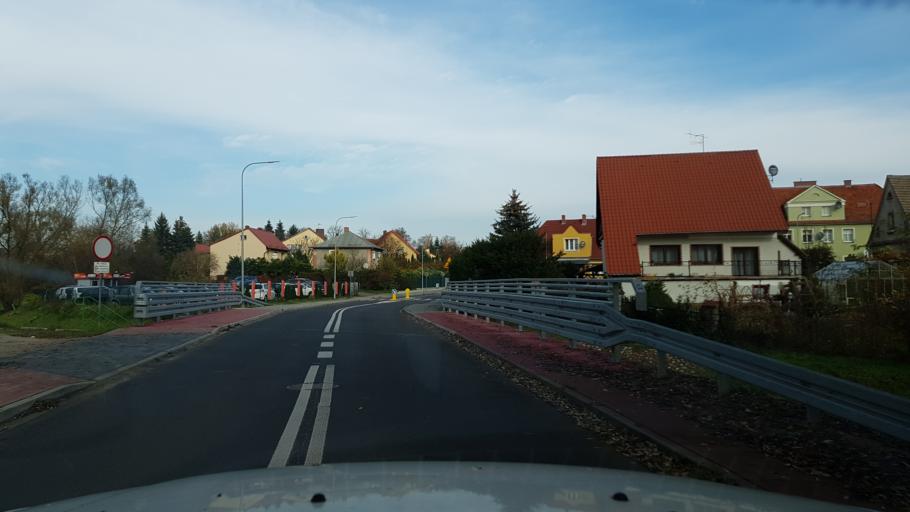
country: PL
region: West Pomeranian Voivodeship
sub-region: Powiat swidwinski
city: Polczyn-Zdroj
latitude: 53.7682
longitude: 16.0903
